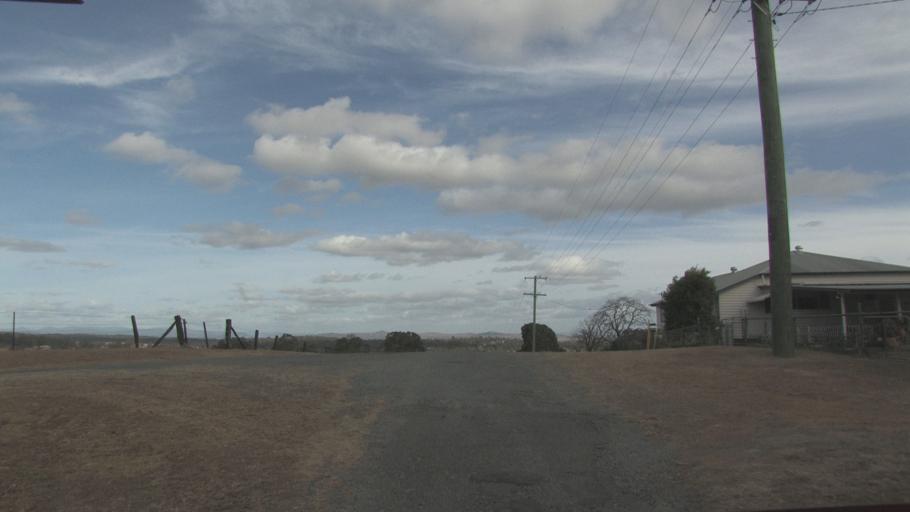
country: AU
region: Queensland
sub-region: Logan
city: Cedar Vale
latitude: -27.9137
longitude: 152.9962
